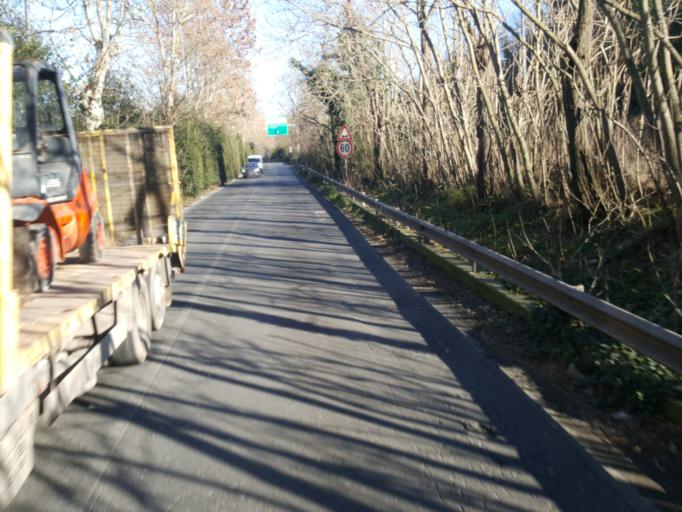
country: IT
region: Latium
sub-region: Citta metropolitana di Roma Capitale
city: Vitinia
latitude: 41.7971
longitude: 12.4120
